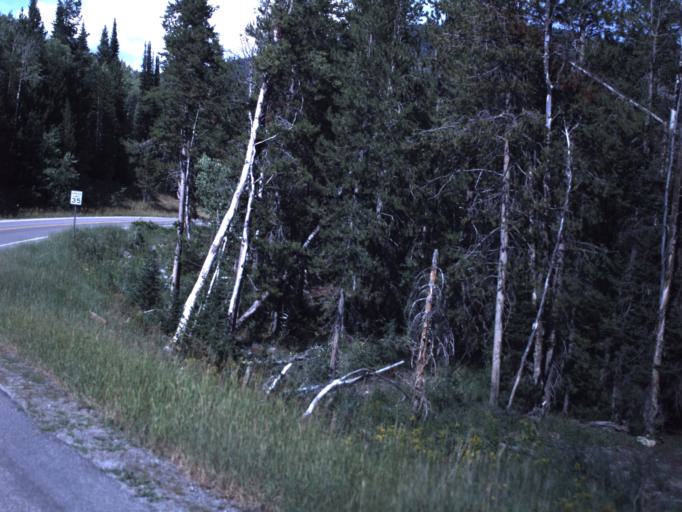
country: US
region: Utah
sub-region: Cache County
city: Richmond
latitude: 41.9705
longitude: -111.5402
